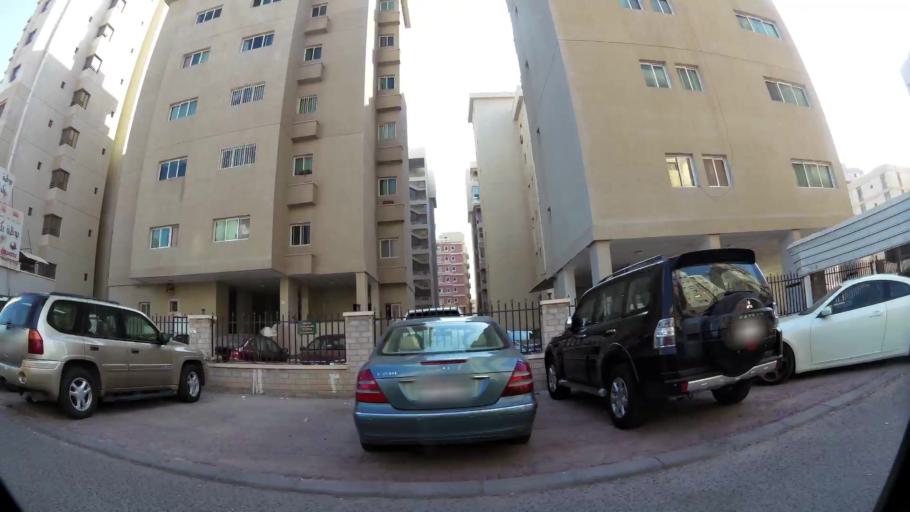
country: KW
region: Muhafazat Hawalli
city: As Salimiyah
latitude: 29.3410
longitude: 48.0939
